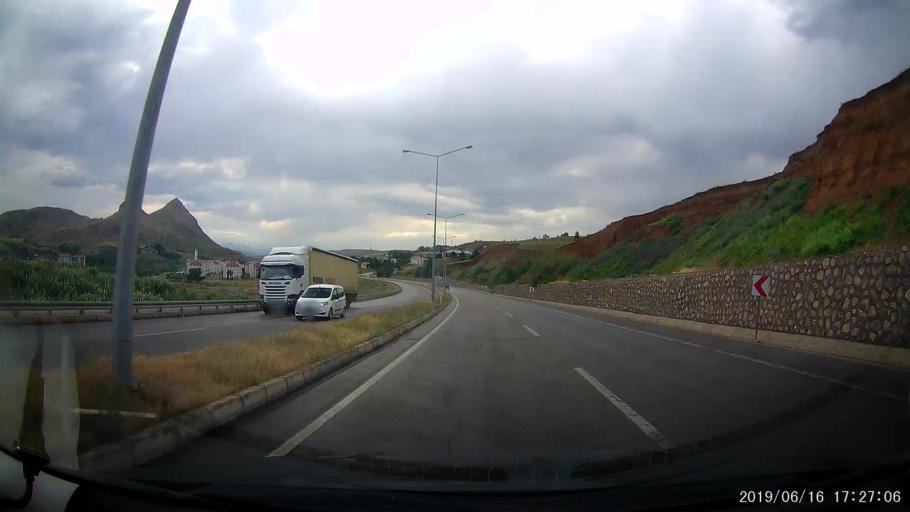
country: TR
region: Erzincan
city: Tercan
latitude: 39.7748
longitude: 40.3994
